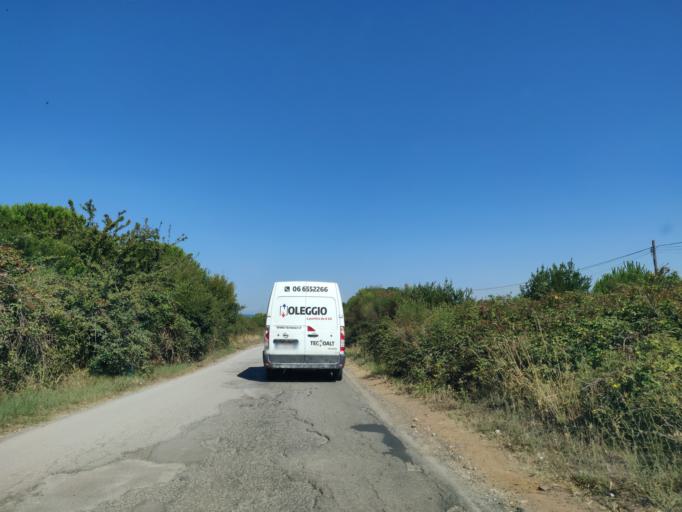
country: IT
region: Latium
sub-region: Citta metropolitana di Roma Capitale
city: Aurelia
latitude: 42.1686
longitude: 11.7422
